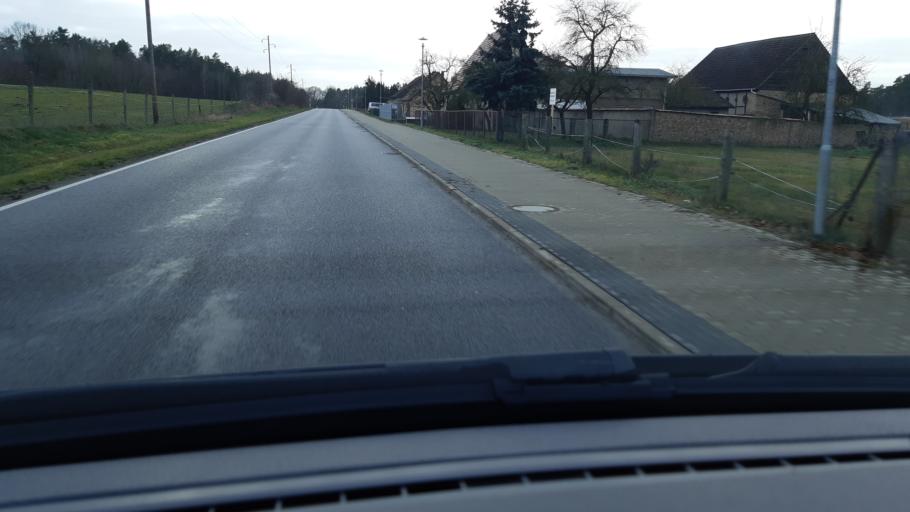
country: DE
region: Brandenburg
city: Templin
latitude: 53.0663
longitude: 13.4235
